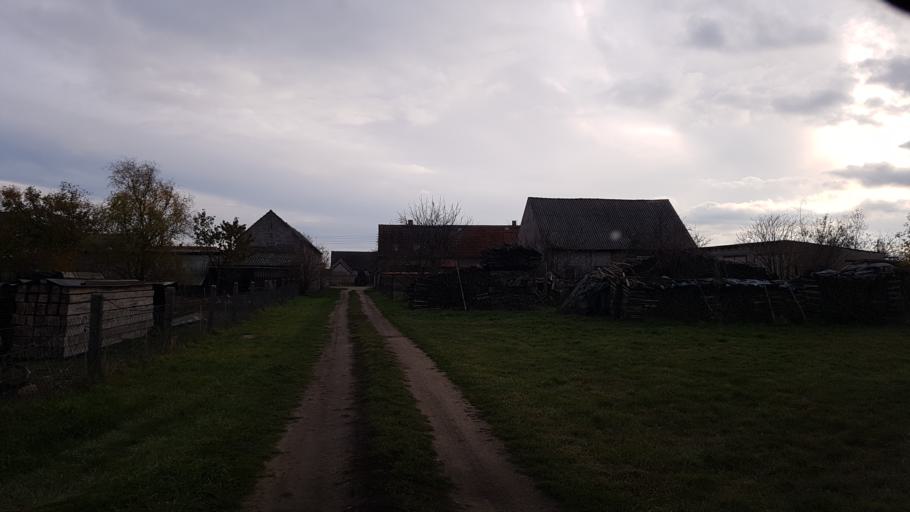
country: DE
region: Brandenburg
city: Trobitz
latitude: 51.6627
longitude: 13.4259
